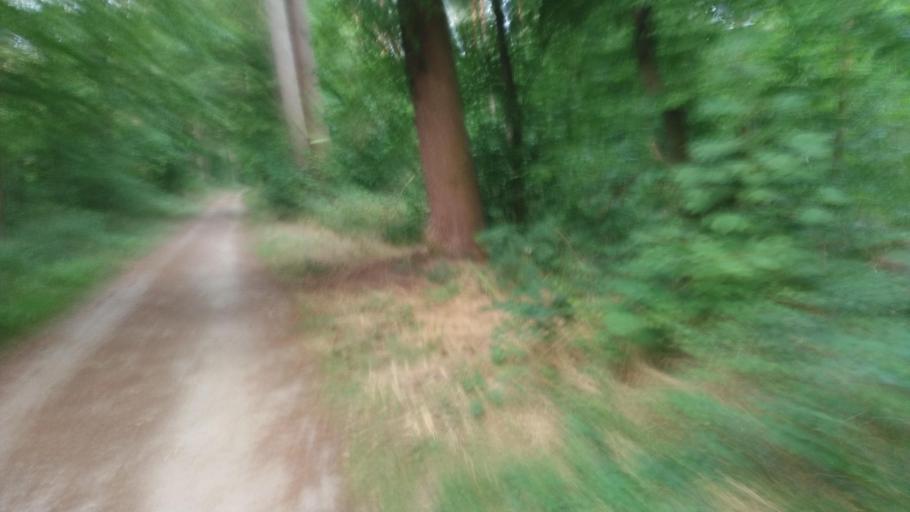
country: DE
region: Baden-Wuerttemberg
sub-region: Karlsruhe Region
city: Bruchsal
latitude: 49.1102
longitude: 8.5639
